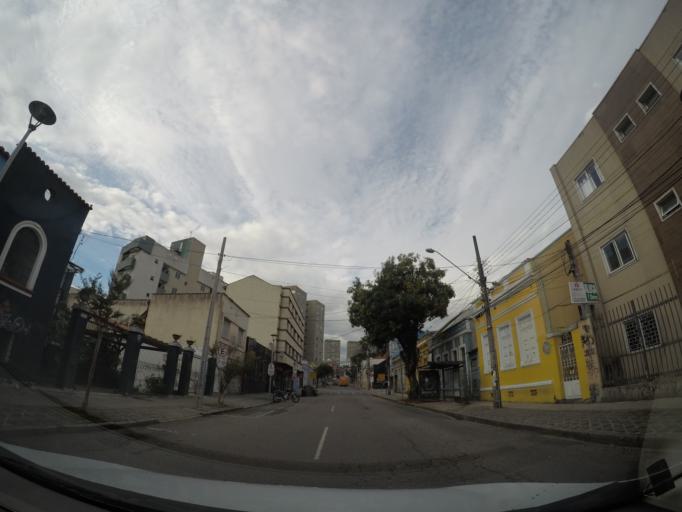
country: BR
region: Parana
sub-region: Curitiba
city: Curitiba
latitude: -25.4241
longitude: -49.2742
